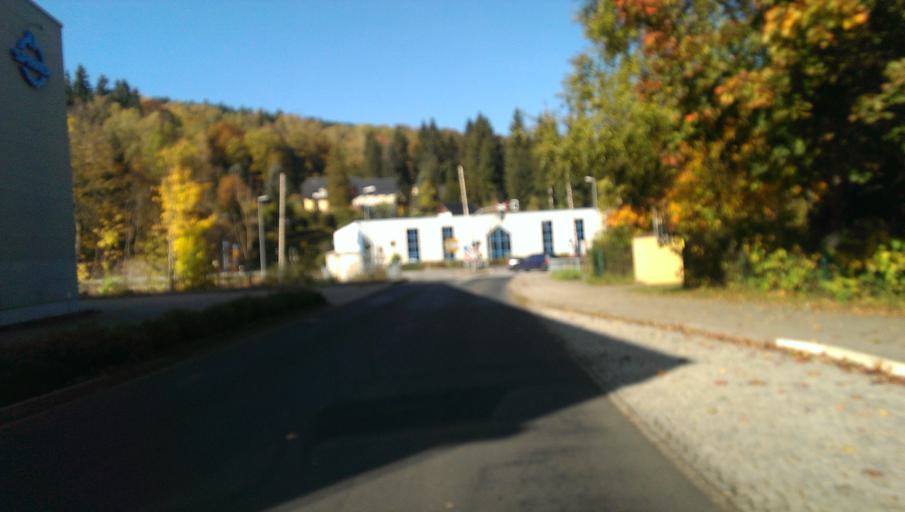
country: DE
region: Saxony
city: Barenstein
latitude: 50.7854
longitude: 13.8144
